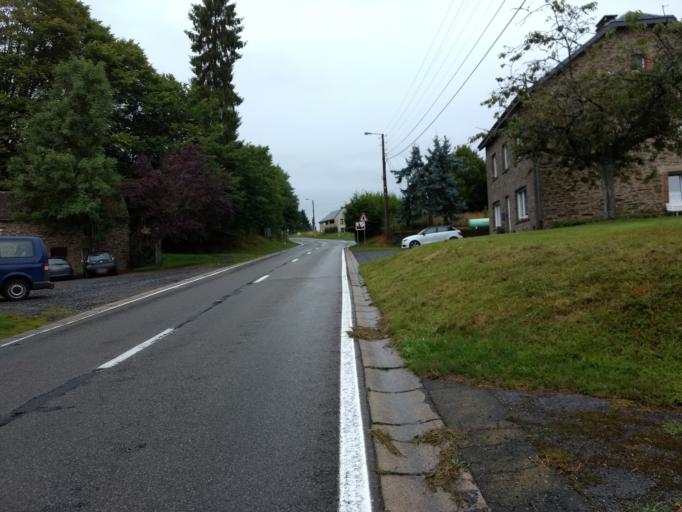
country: BE
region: Wallonia
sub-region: Province du Luxembourg
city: Houffalize
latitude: 50.1463
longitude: 5.7189
